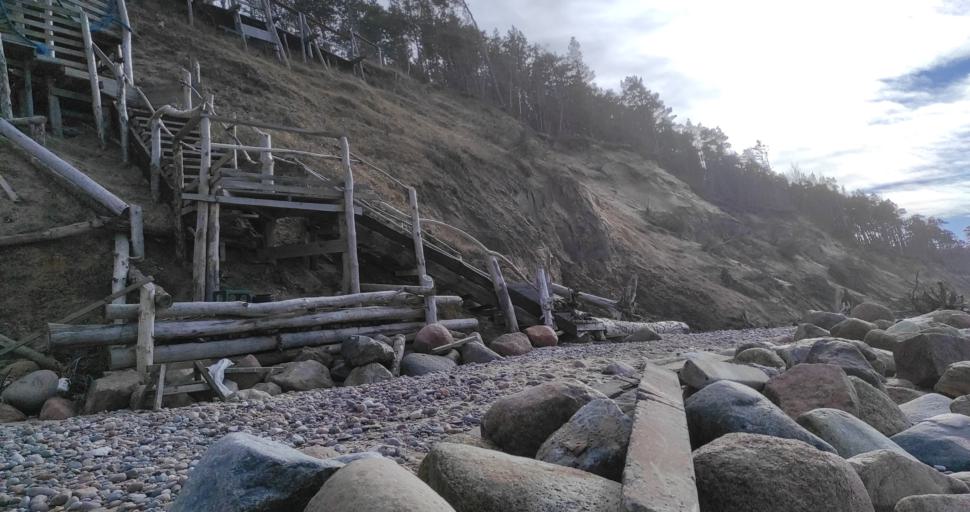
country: LV
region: Alsunga
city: Alsunga
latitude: 57.0292
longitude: 21.3969
